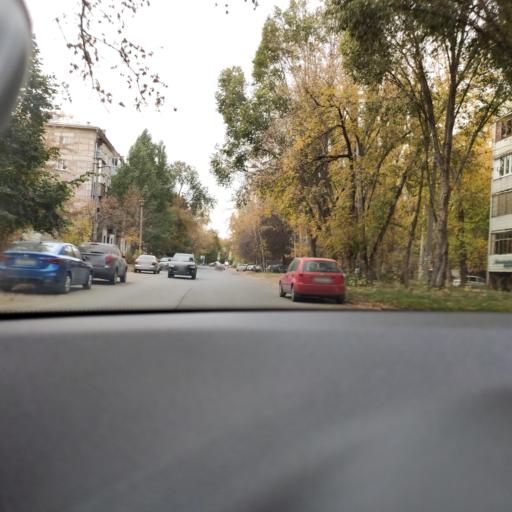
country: RU
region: Samara
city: Samara
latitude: 53.2336
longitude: 50.2481
